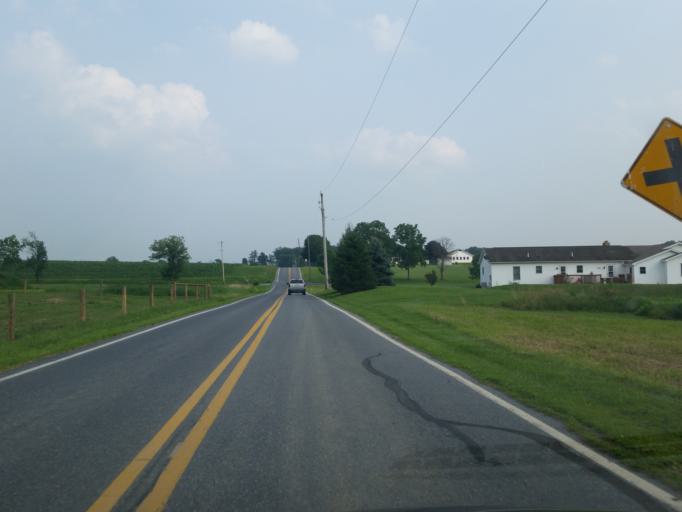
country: US
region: Pennsylvania
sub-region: Lebanon County
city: Palmyra
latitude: 40.4030
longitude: -76.6369
